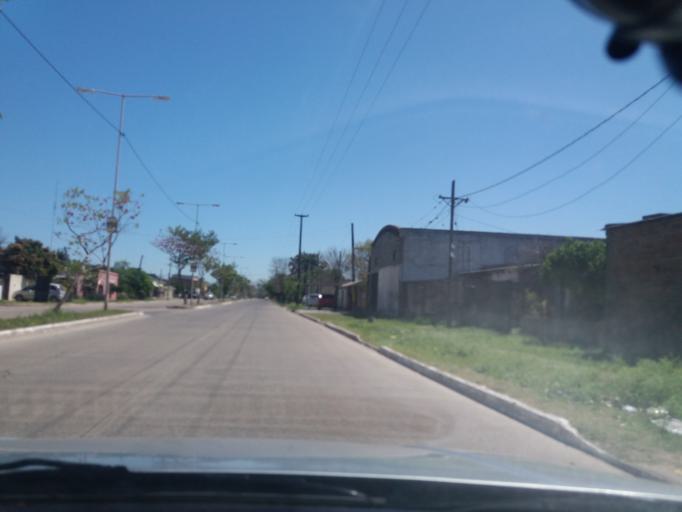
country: AR
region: Corrientes
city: Corrientes
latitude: -27.4887
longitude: -58.8408
